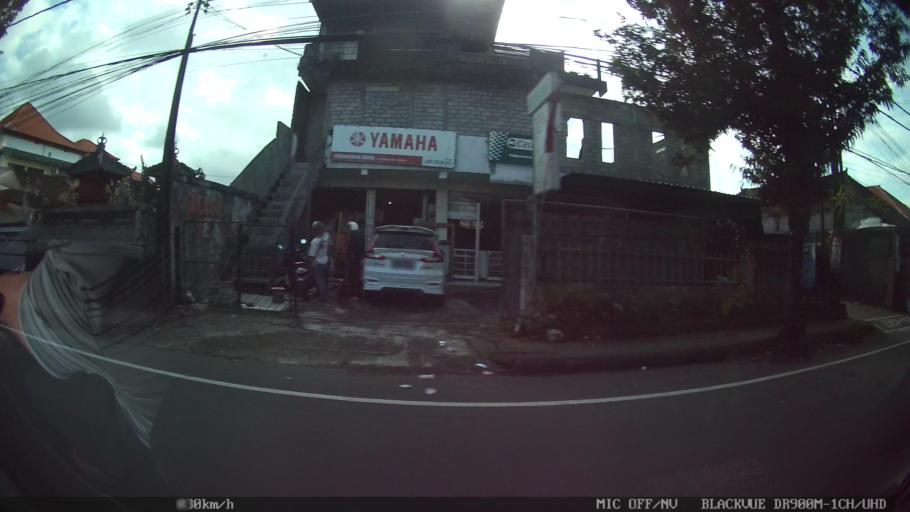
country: ID
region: Bali
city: Tabanan
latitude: -8.5483
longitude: 115.1240
